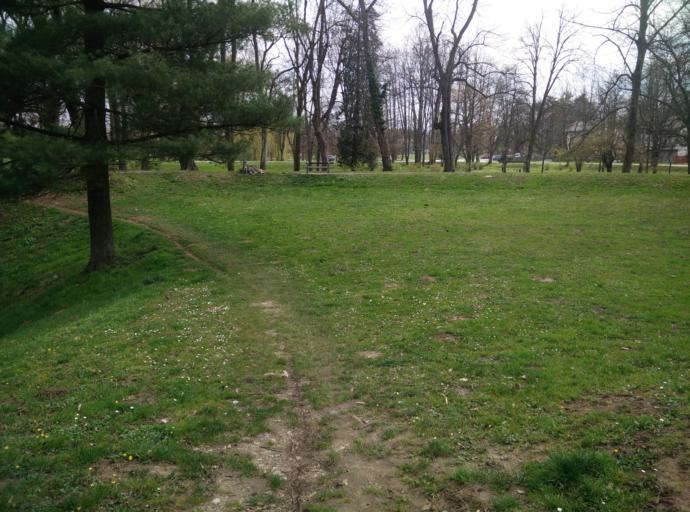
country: HR
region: Karlovacka
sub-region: Grad Karlovac
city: Karlovac
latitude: 45.4906
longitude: 15.5585
